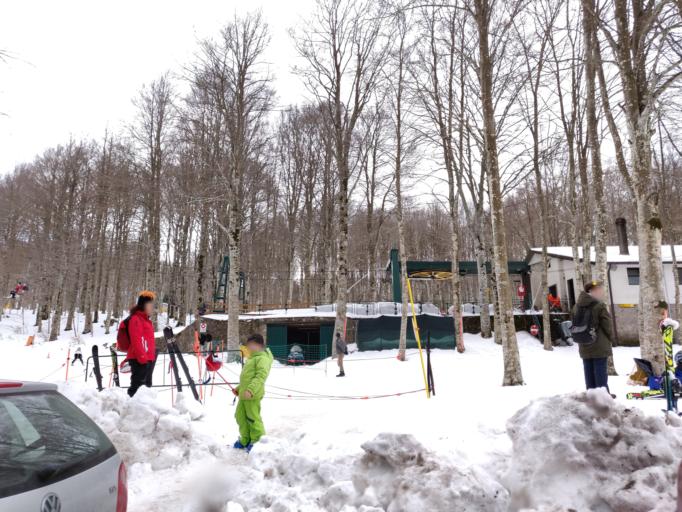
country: IT
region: Tuscany
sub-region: Provincia di Grosseto
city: Seggiano
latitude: 42.8908
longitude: 11.6071
